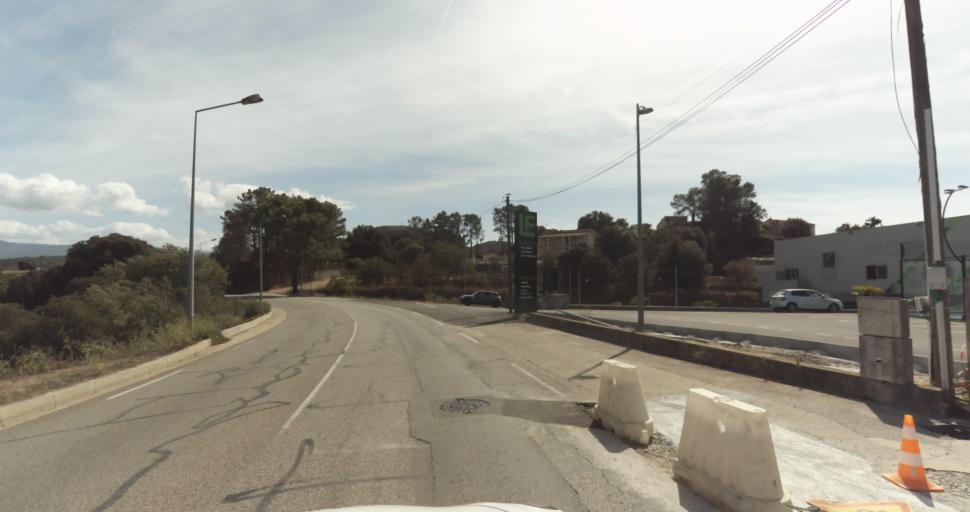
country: FR
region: Corsica
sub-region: Departement de la Corse-du-Sud
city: Afa
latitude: 41.9563
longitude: 8.7821
